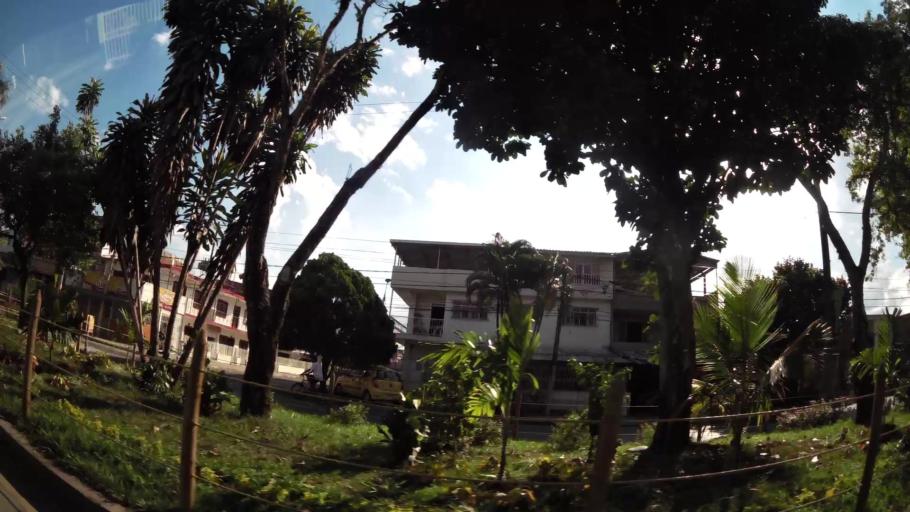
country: CO
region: Valle del Cauca
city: Cali
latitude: 3.4055
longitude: -76.5082
